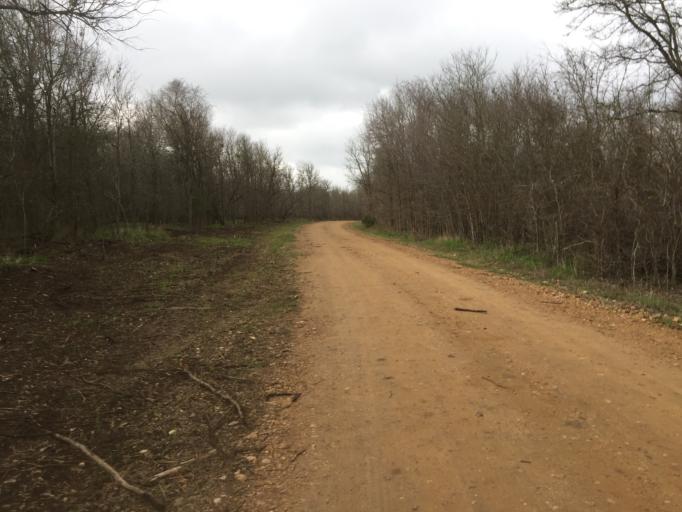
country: US
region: Texas
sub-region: Bastrop County
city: Bastrop
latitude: 30.0836
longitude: -97.3222
